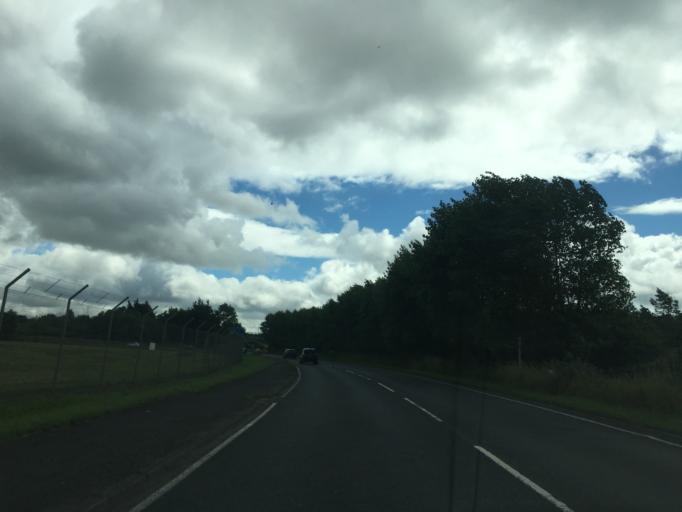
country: GB
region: Scotland
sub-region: Renfrewshire
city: Inchinnan
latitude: 55.8602
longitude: -4.4548
